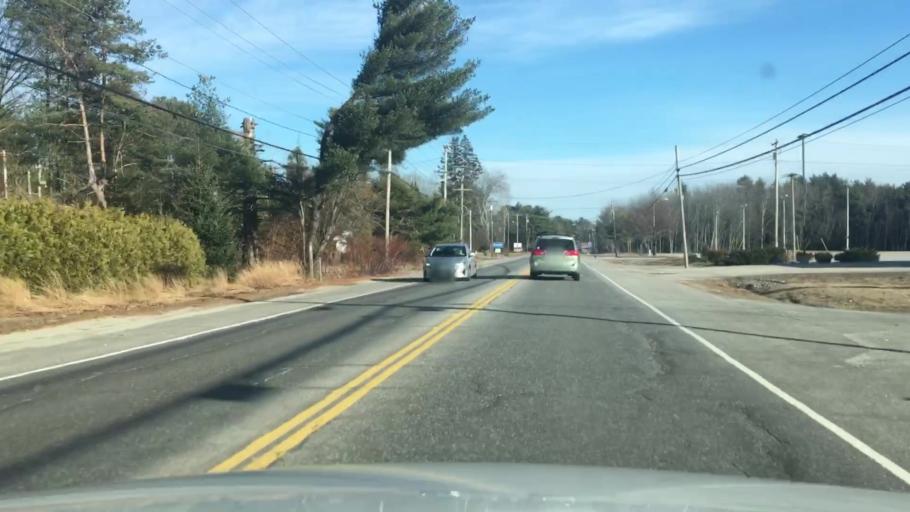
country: US
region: Maine
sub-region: Cumberland County
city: Brunswick
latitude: 43.9108
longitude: -69.9023
